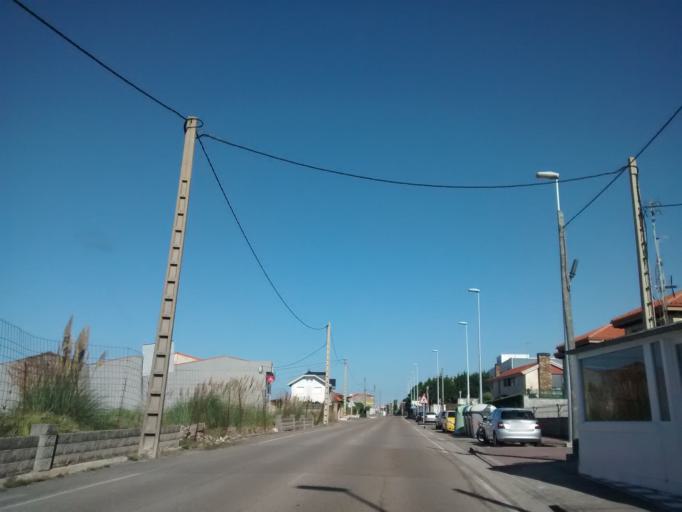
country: ES
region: Cantabria
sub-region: Provincia de Cantabria
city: Santander
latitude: 43.4654
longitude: -3.8510
